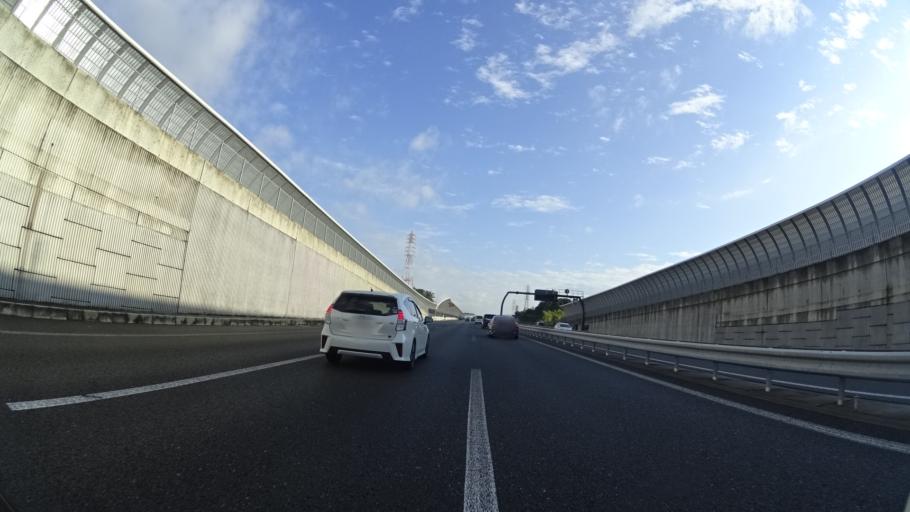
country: JP
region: Osaka
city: Neyagawa
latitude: 34.7596
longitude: 135.6477
